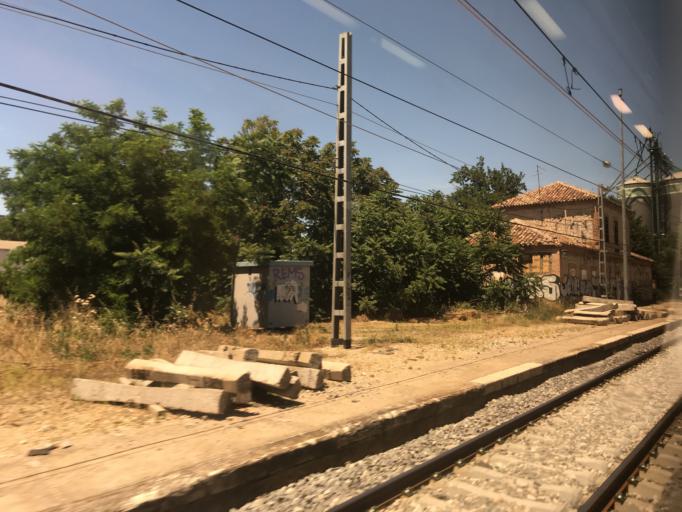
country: ES
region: Madrid
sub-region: Provincia de Madrid
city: Ciempozuelos
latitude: 40.0952
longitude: -3.6289
